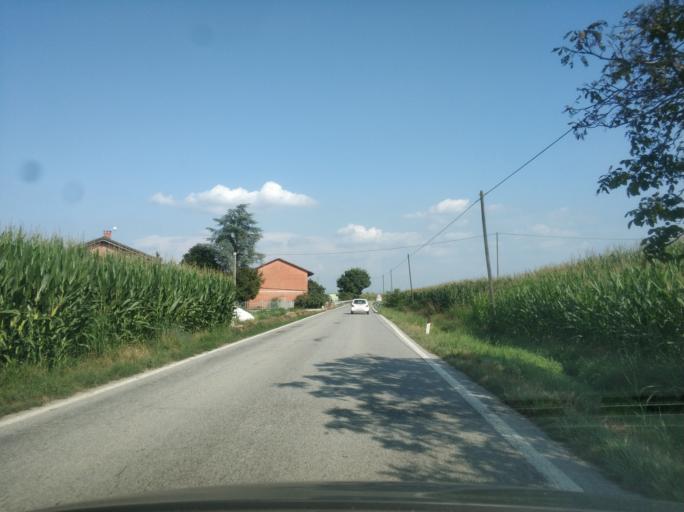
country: IT
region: Piedmont
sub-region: Provincia di Cuneo
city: Centallo
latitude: 44.5332
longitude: 7.6357
